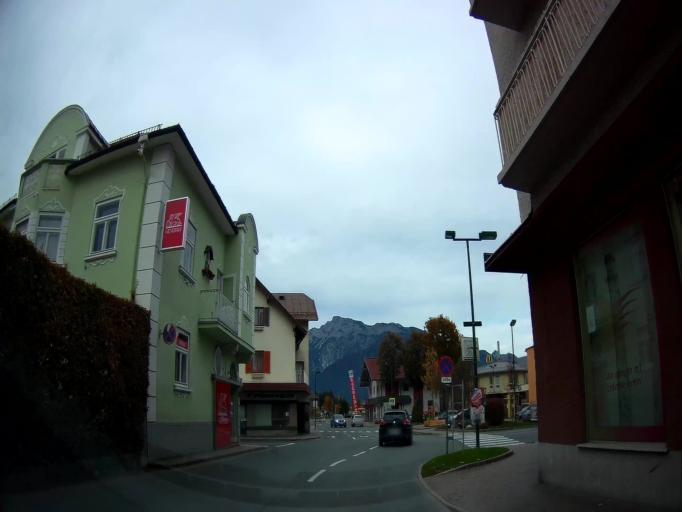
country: AT
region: Salzburg
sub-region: Politischer Bezirk Zell am See
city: Saalfelden am Steinernen Meer
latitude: 47.4284
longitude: 12.8443
